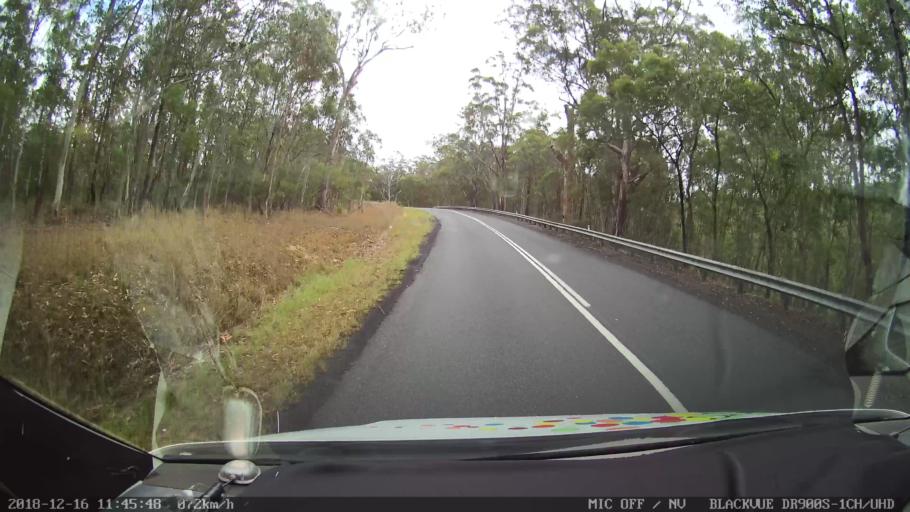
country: AU
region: New South Wales
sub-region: Tenterfield Municipality
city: Carrolls Creek
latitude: -28.9326
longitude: 152.2260
